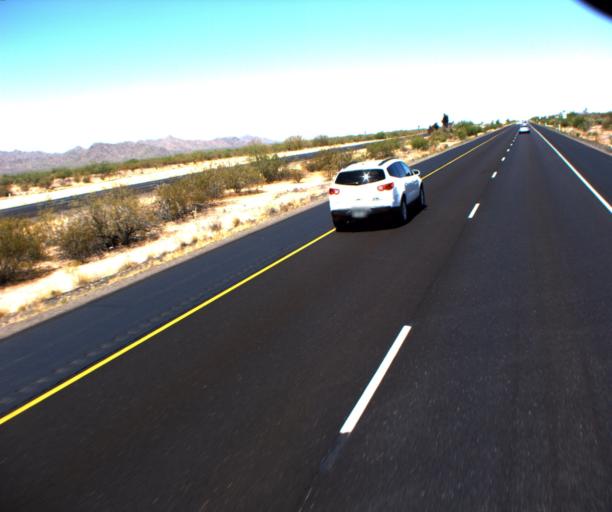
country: US
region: Arizona
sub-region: Yavapai County
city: Congress
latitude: 34.0795
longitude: -112.8874
